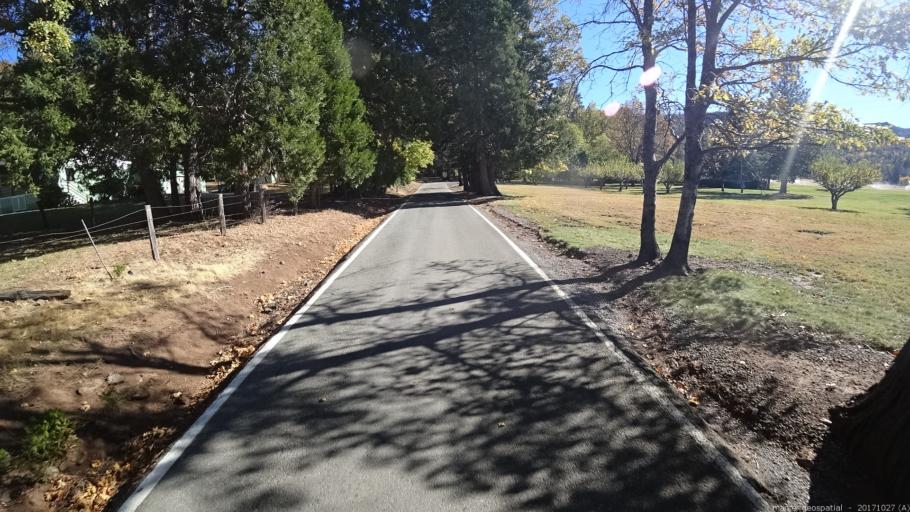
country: US
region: California
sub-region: Shasta County
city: Burney
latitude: 40.8055
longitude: -121.8920
